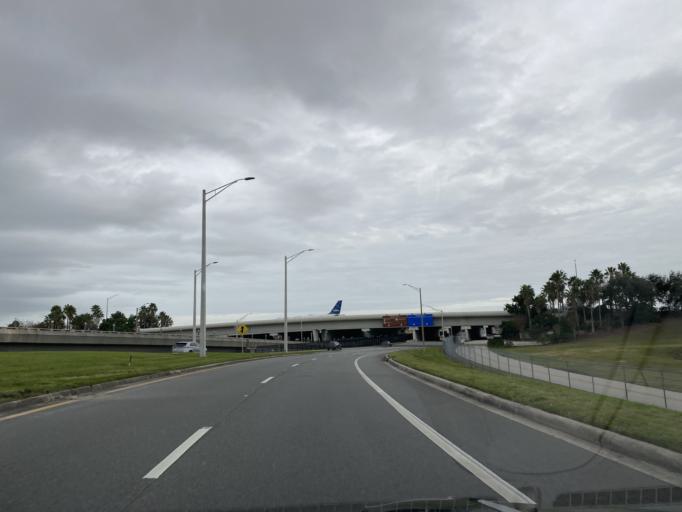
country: US
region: Florida
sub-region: Orange County
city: Taft
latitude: 28.4255
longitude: -81.3073
